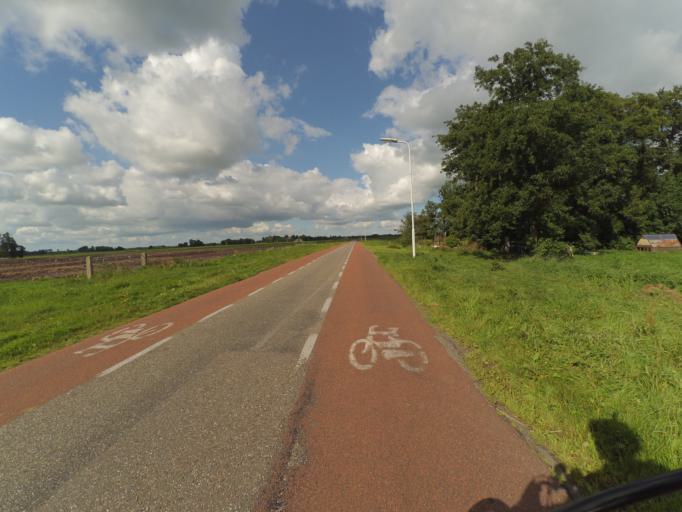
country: NL
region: Friesland
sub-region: Gemeente Dantumadiel
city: Rinsumageast
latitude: 53.2598
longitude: 5.9454
